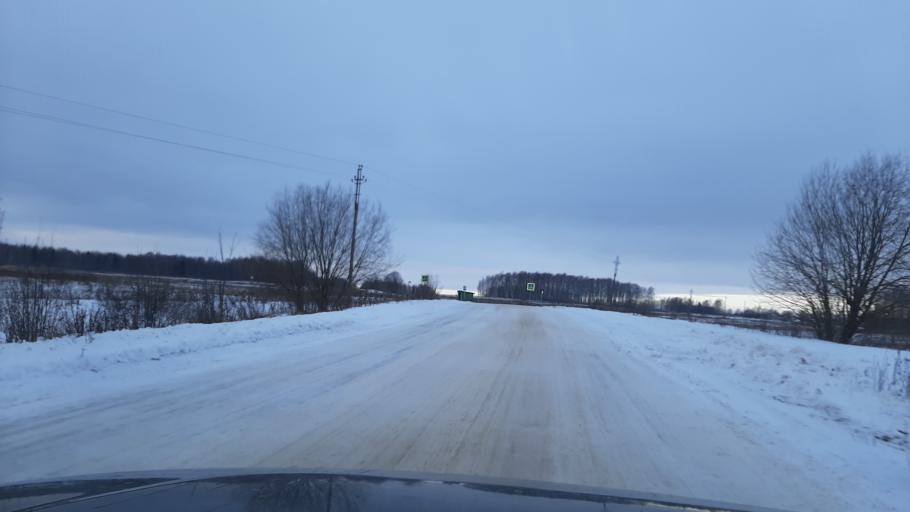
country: RU
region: Kostroma
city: Volgorechensk
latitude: 57.4495
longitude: 41.0271
